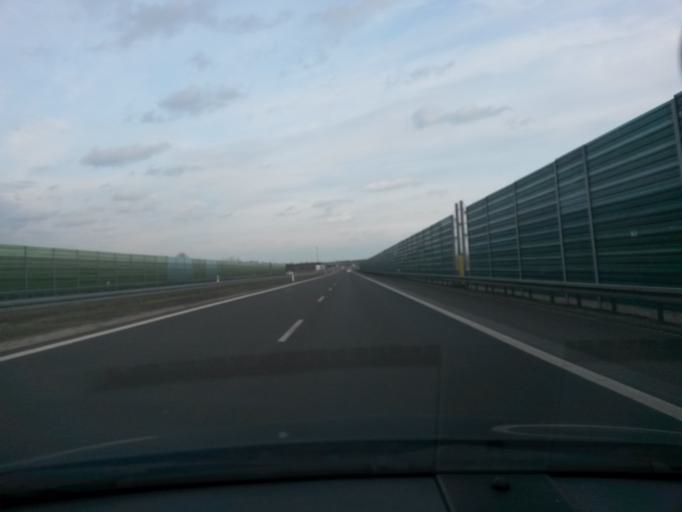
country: PL
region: Greater Poland Voivodeship
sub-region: Powiat kolski
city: Grzegorzew
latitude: 52.1205
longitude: 18.6984
